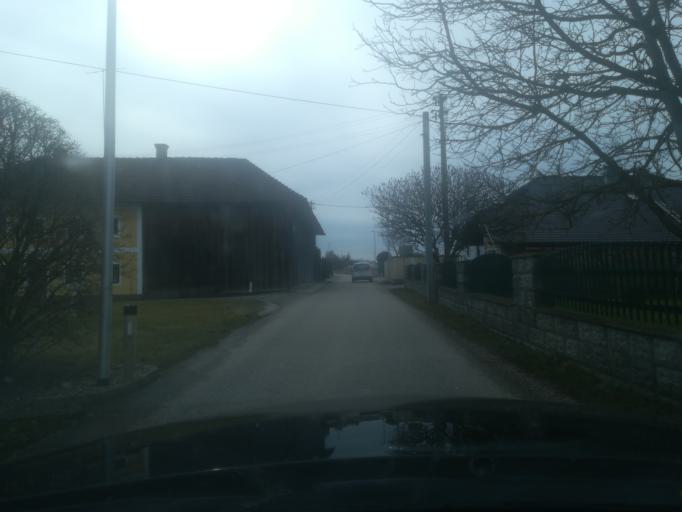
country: AT
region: Upper Austria
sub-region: Wels-Land
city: Bad Wimsbach-Neydharting
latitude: 48.0997
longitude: 13.9231
